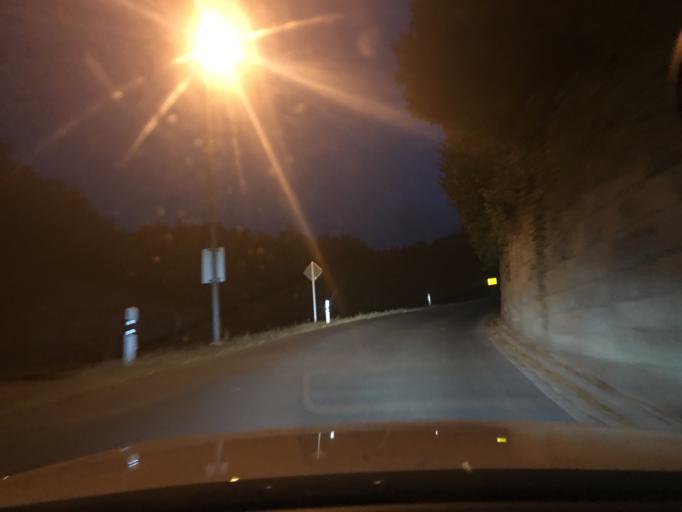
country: DE
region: Bavaria
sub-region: Upper Franconia
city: Prebitz
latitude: 49.7969
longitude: 11.6501
